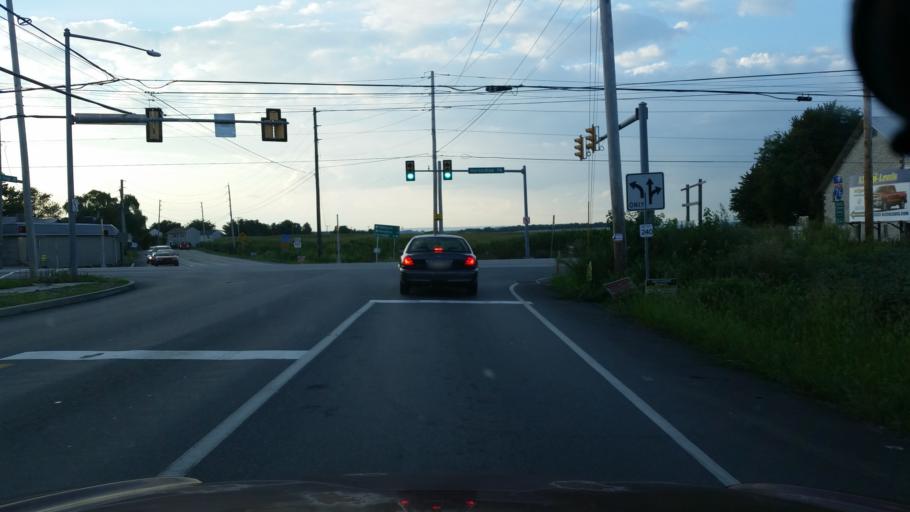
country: US
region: Pennsylvania
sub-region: Lebanon County
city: Campbelltown
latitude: 40.2783
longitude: -76.5705
